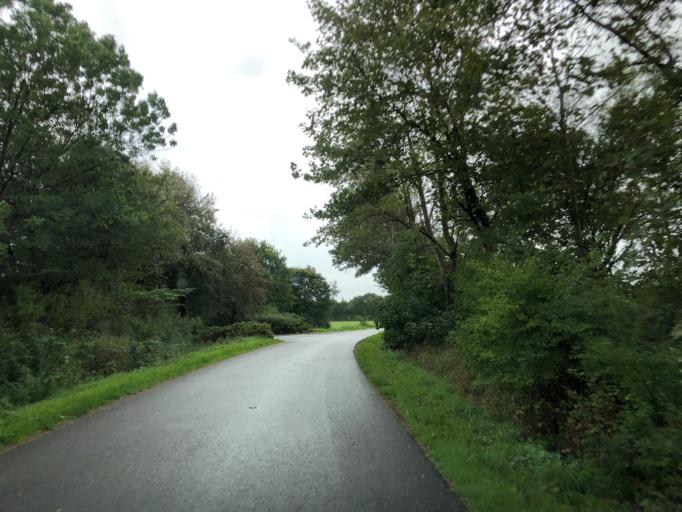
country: DK
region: Central Jutland
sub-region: Herning Kommune
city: Vildbjerg
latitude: 56.1943
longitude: 8.8022
